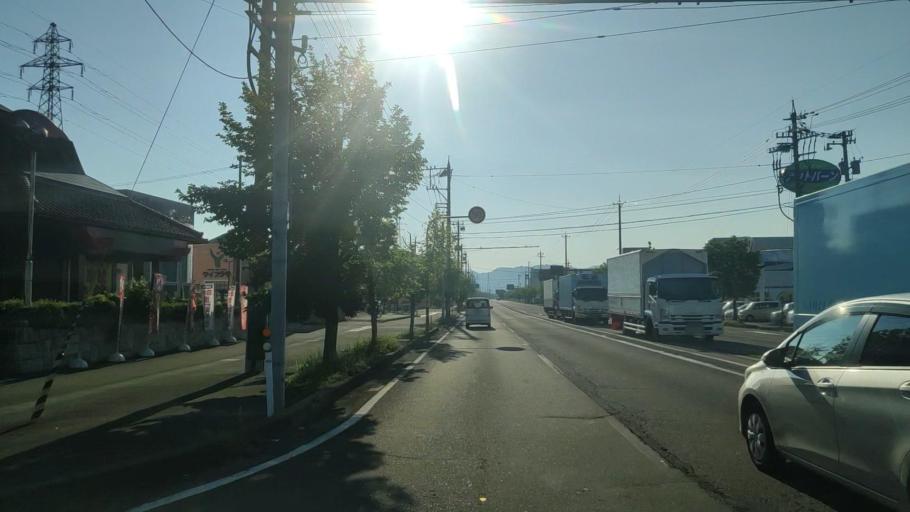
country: JP
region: Fukui
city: Fukui-shi
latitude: 36.0855
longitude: 136.2477
